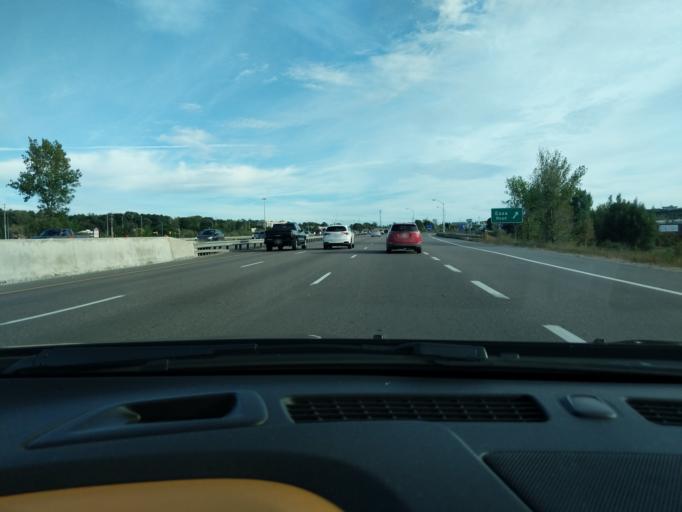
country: CA
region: Ontario
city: Barrie
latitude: 44.3655
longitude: -79.7015
